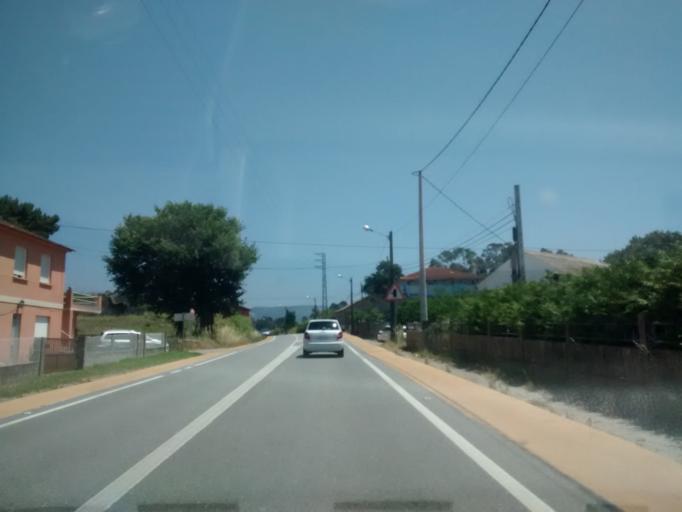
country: ES
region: Galicia
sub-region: Provincia de Pontevedra
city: Nigran
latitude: 42.1139
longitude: -8.7945
